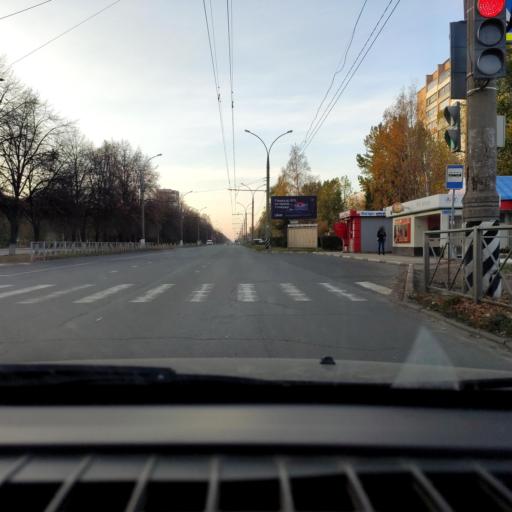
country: RU
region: Samara
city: Tol'yatti
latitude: 53.5364
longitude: 49.2779
